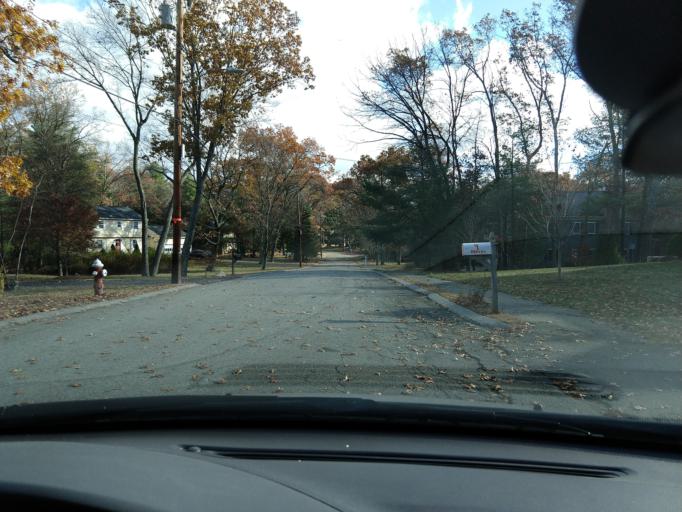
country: US
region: Massachusetts
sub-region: Middlesex County
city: Bedford
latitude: 42.4911
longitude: -71.2437
